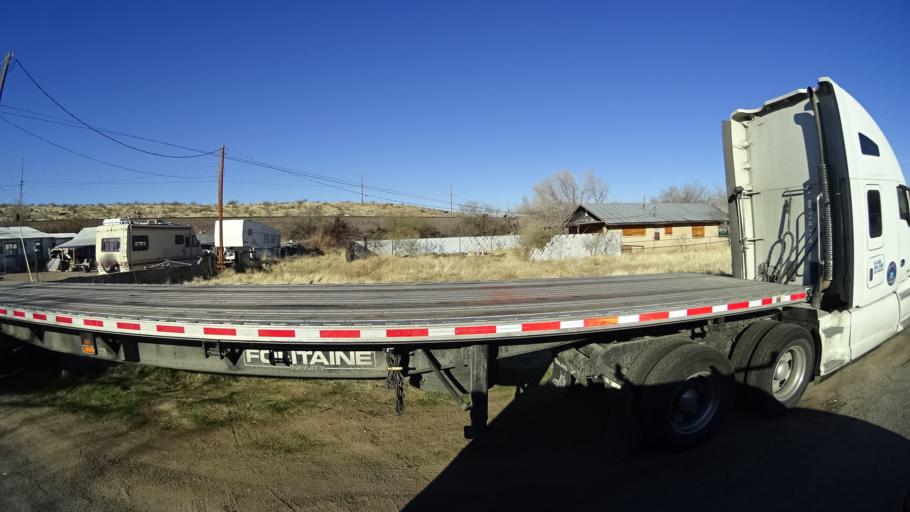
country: US
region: Arizona
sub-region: Mohave County
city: Kingman
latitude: 35.1839
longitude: -114.0444
